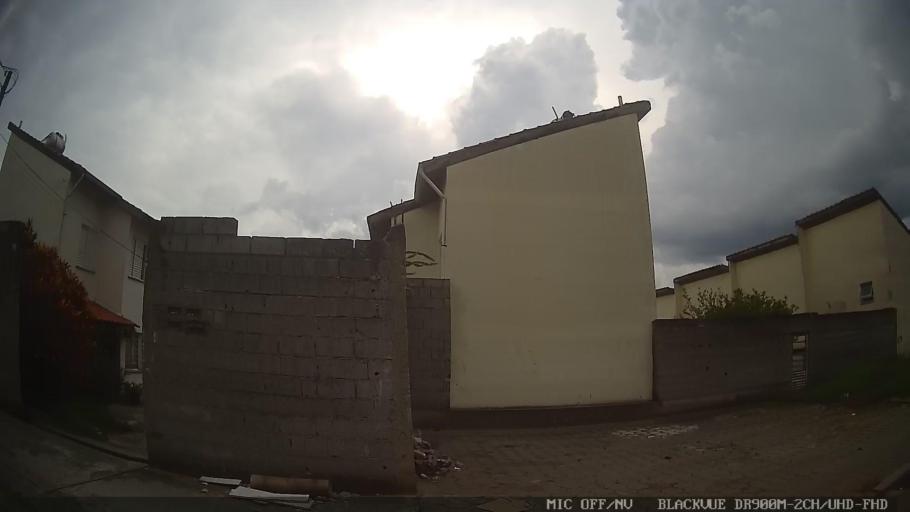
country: BR
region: Sao Paulo
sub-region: Atibaia
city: Atibaia
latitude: -23.1256
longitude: -46.5882
